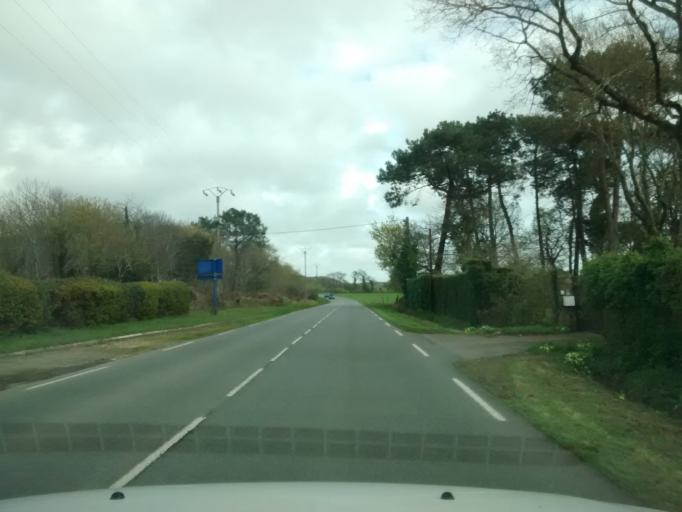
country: FR
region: Brittany
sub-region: Departement du Finistere
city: Clohars-Carnoet
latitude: 47.7987
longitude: -3.5500
